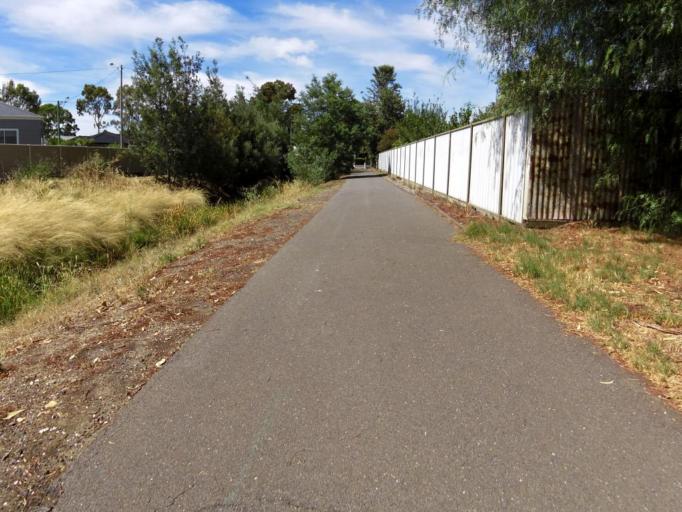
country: AU
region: Victoria
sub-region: Greater Bendigo
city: White Hills
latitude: -36.7414
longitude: 144.2963
